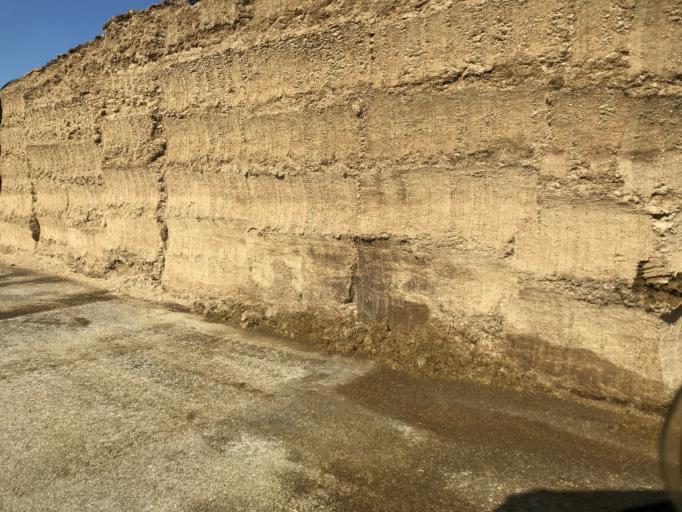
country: GB
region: England
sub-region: Cheshire West and Chester
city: Aldford
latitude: 53.1250
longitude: -2.8488
